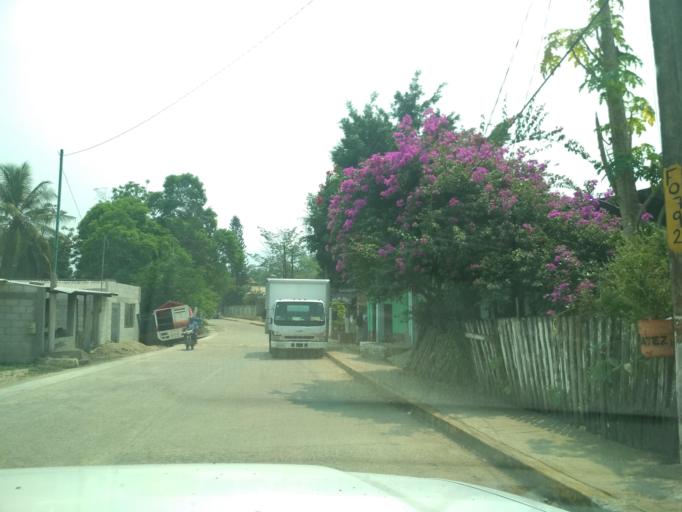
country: MX
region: Veracruz
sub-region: Tezonapa
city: Laguna Chica (Pueblo Nuevo)
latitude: 18.5436
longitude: -96.7791
